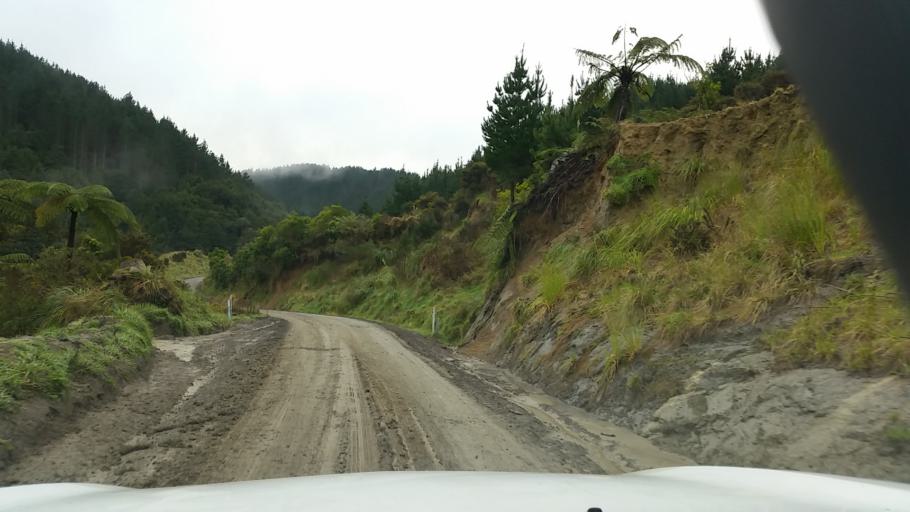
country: NZ
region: Taranaki
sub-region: South Taranaki District
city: Hawera
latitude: -39.5241
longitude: 174.4124
